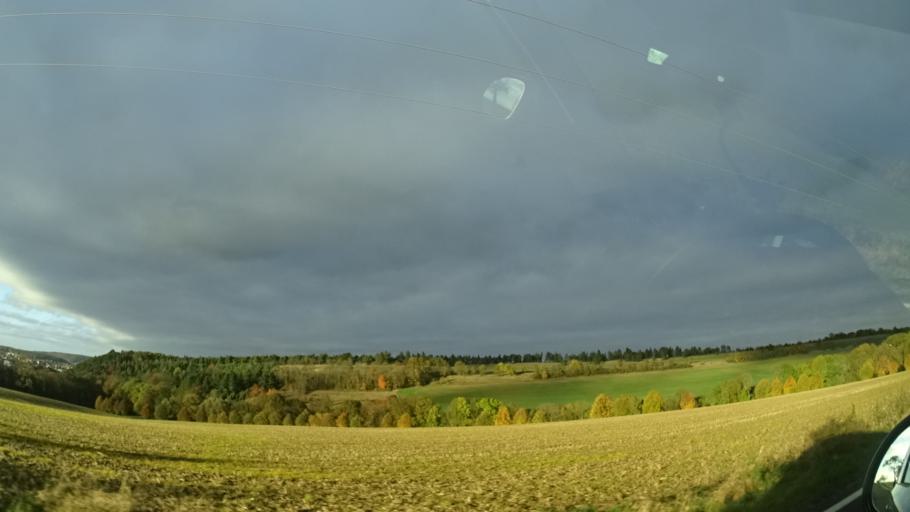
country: DE
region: Thuringia
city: Blankenhain
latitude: 50.8415
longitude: 11.3644
